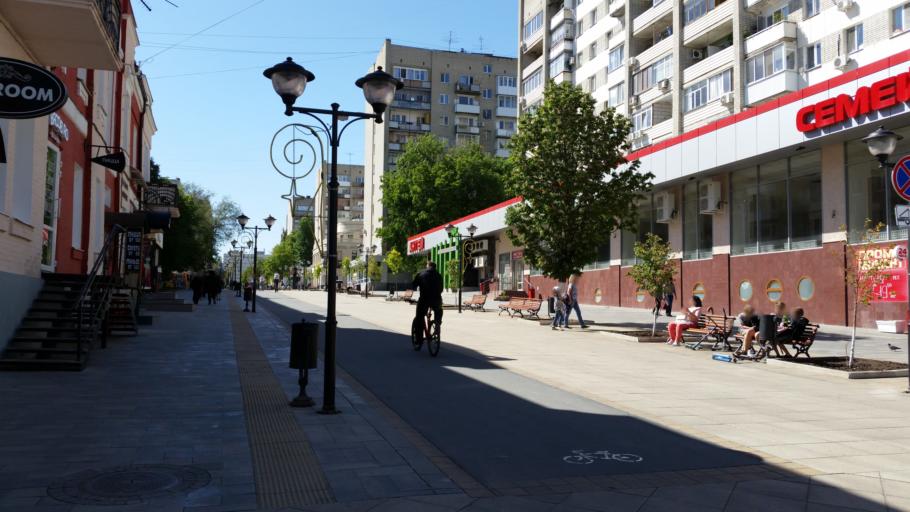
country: RU
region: Saratov
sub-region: Saratovskiy Rayon
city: Saratov
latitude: 51.5283
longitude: 46.0443
